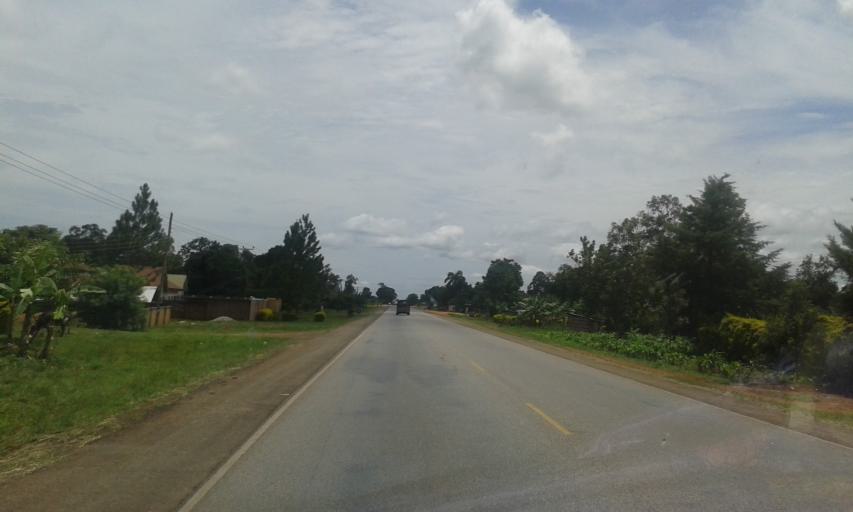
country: UG
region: Eastern Region
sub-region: Iganga District
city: Iganga
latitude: 0.5484
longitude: 33.4036
